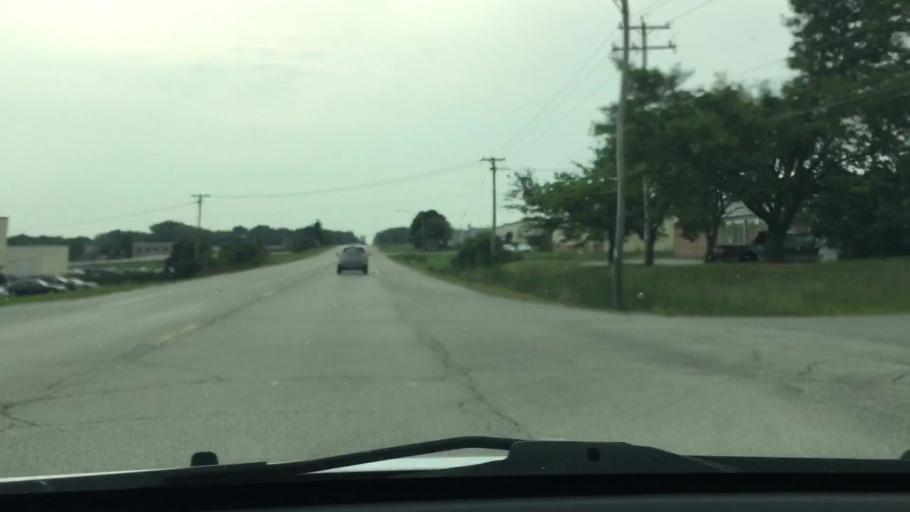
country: US
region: Wisconsin
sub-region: Waukesha County
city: New Berlin
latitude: 42.9952
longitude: -88.1194
